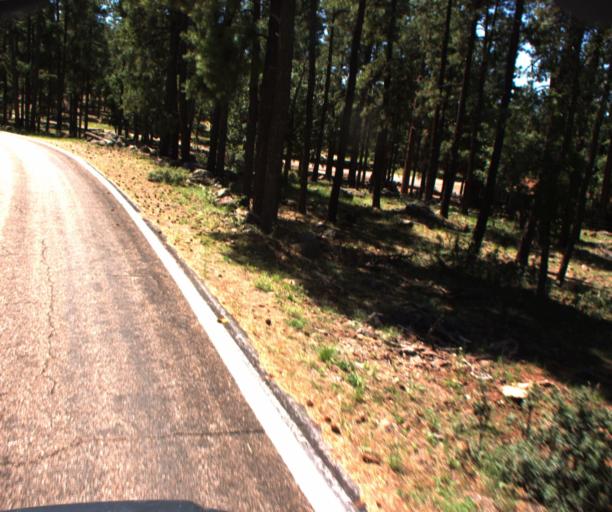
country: US
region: Arizona
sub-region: Greenlee County
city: Morenci
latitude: 33.5418
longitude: -109.3171
